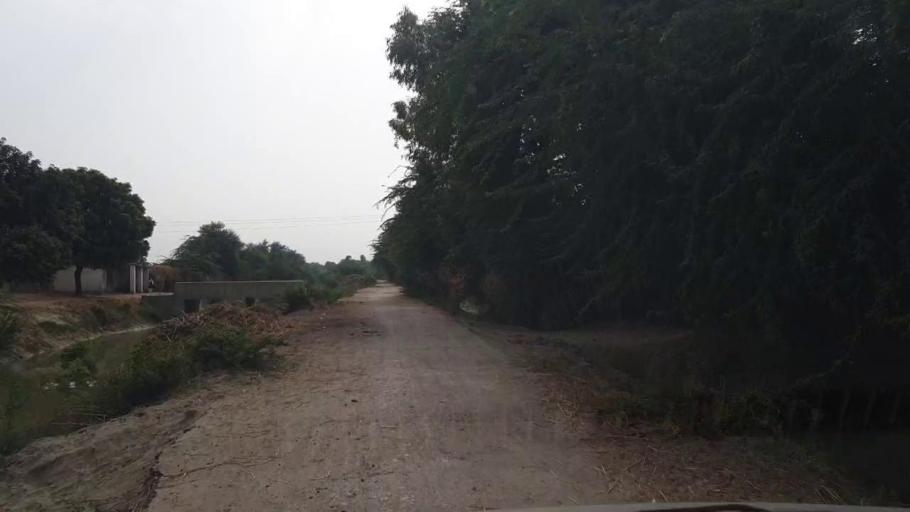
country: PK
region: Sindh
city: Matli
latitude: 25.0022
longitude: 68.7015
